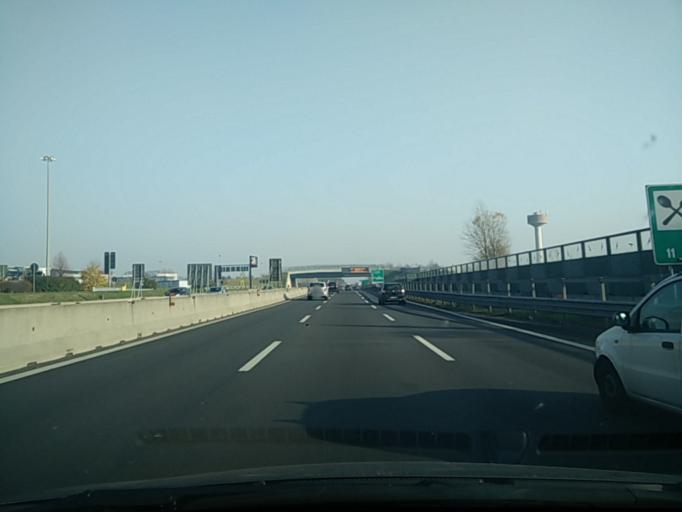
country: IT
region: Lombardy
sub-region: Citta metropolitana di Milano
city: Pero
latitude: 45.5131
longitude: 9.0697
